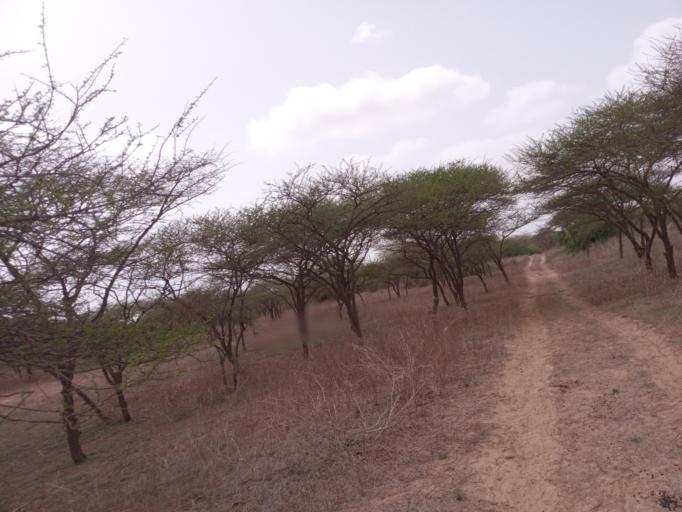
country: SN
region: Saint-Louis
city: Saint-Louis
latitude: 15.9239
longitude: -16.4535
